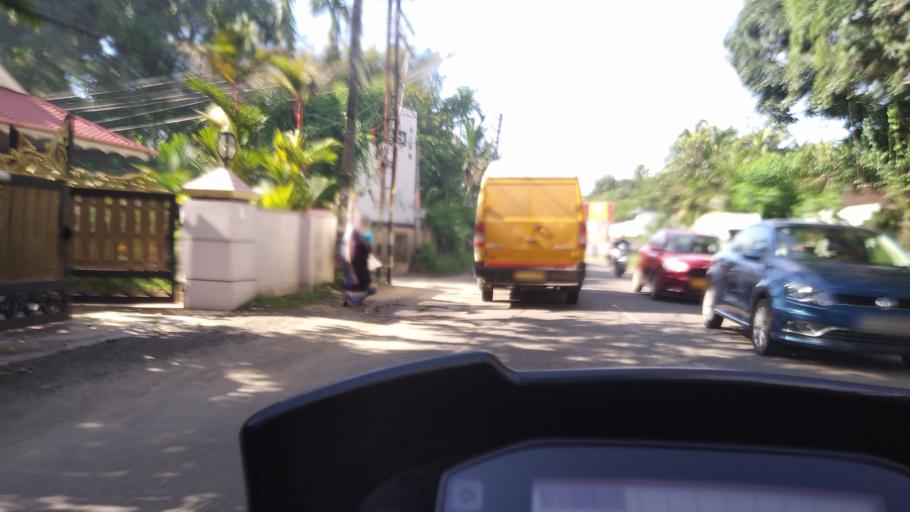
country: IN
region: Kerala
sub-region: Ernakulam
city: Elur
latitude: 10.0317
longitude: 76.2217
